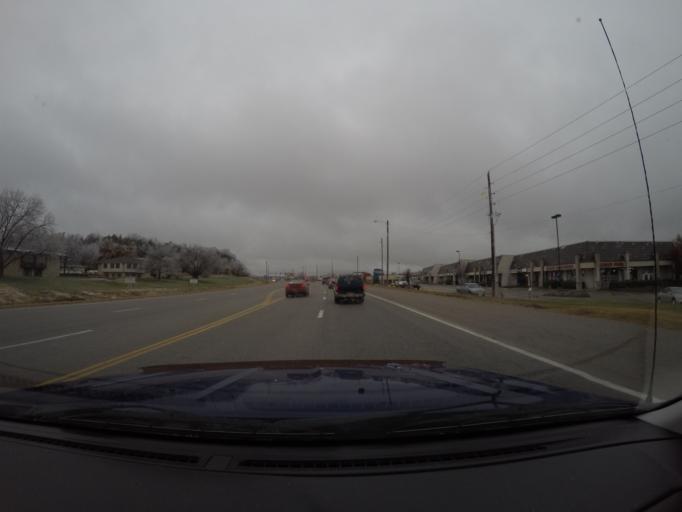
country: US
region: Kansas
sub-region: Riley County
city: Manhattan
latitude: 39.1745
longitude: -96.6037
